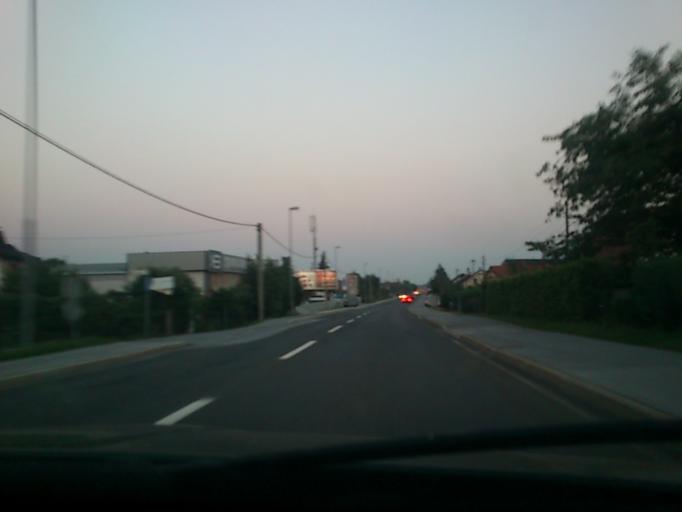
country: SI
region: Miklavz na Dravskem Polju
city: Miklavz na Dravskem Polju
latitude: 46.5074
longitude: 15.6963
